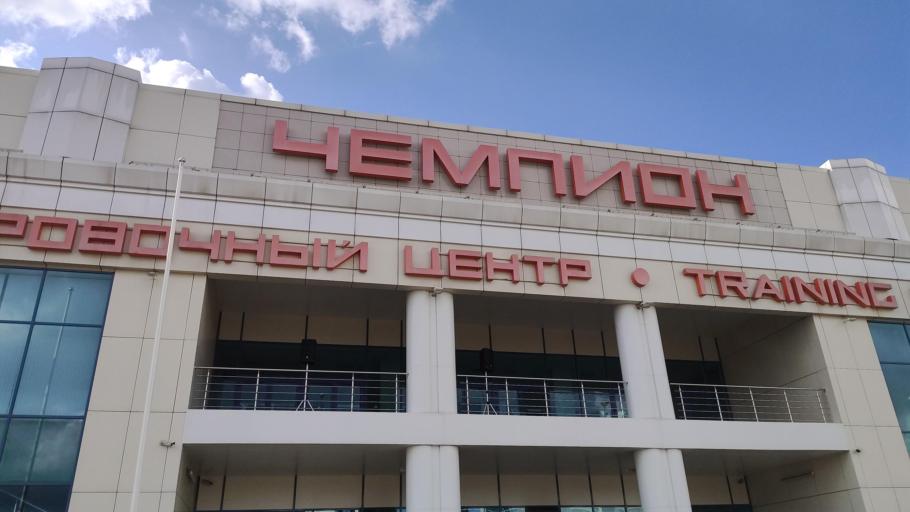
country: RU
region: Krasnodarskiy
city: Krasnodar
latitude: 45.1170
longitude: 38.9780
